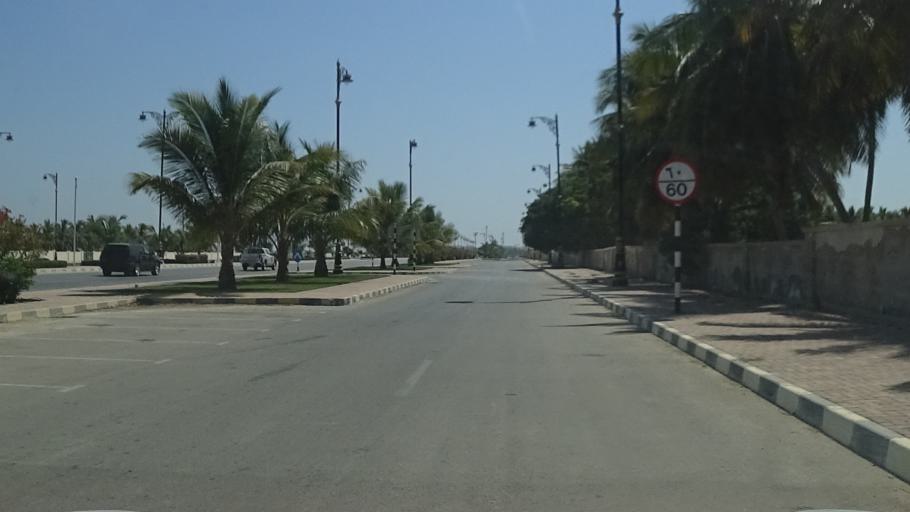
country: OM
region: Zufar
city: Salalah
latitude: 17.0330
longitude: 54.1719
